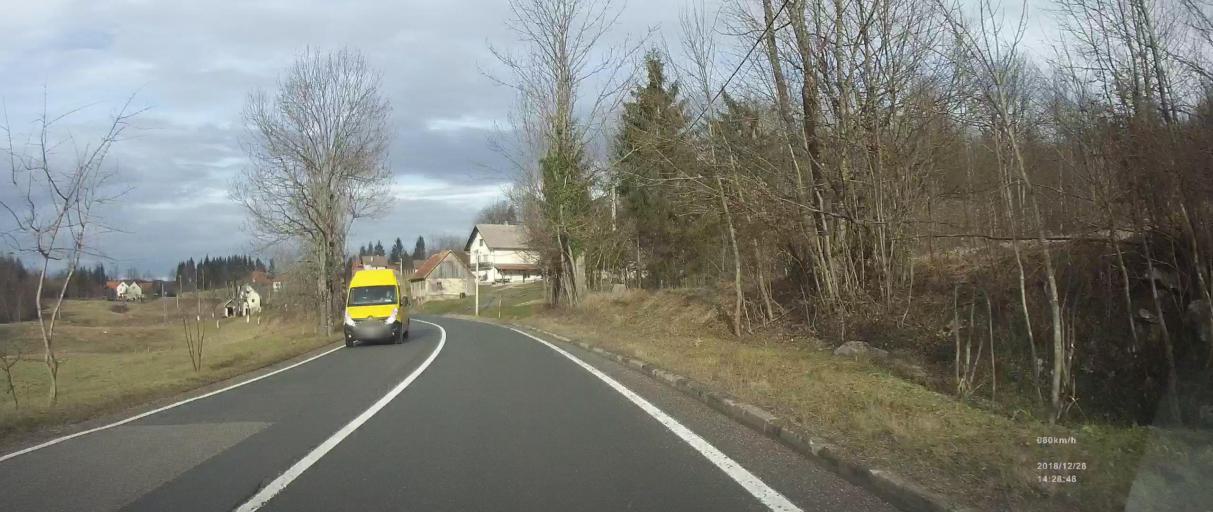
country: HR
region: Primorsko-Goranska
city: Vrbovsko
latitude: 45.4139
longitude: 15.1169
